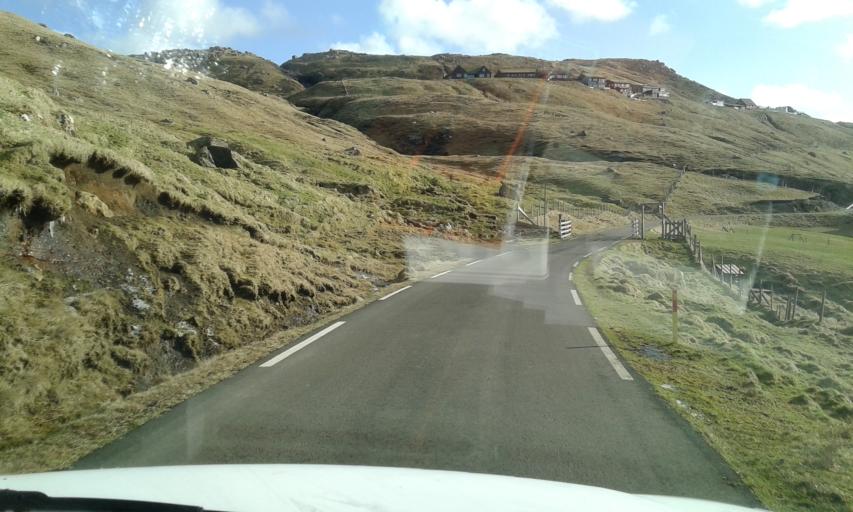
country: FO
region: Streymoy
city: Argir
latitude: 61.9884
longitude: -6.8696
